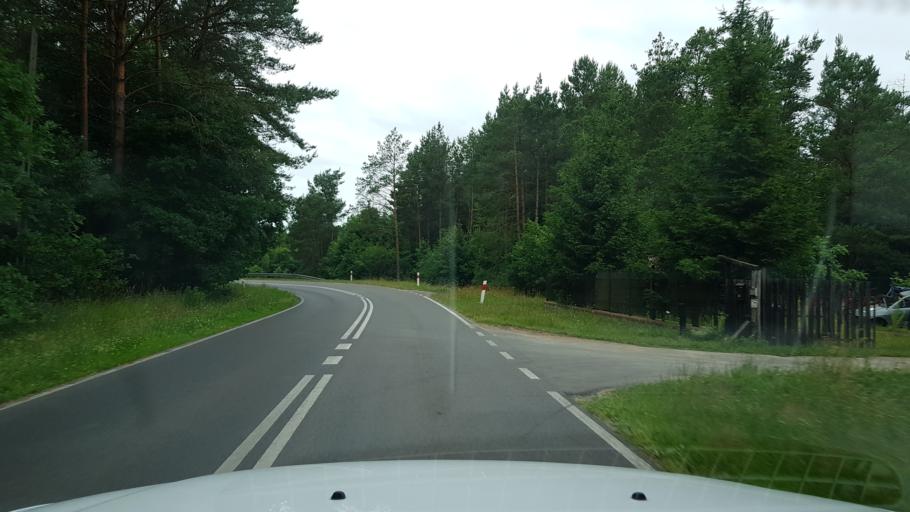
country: PL
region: West Pomeranian Voivodeship
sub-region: Powiat gryficki
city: Brojce
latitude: 53.9549
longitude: 15.3772
